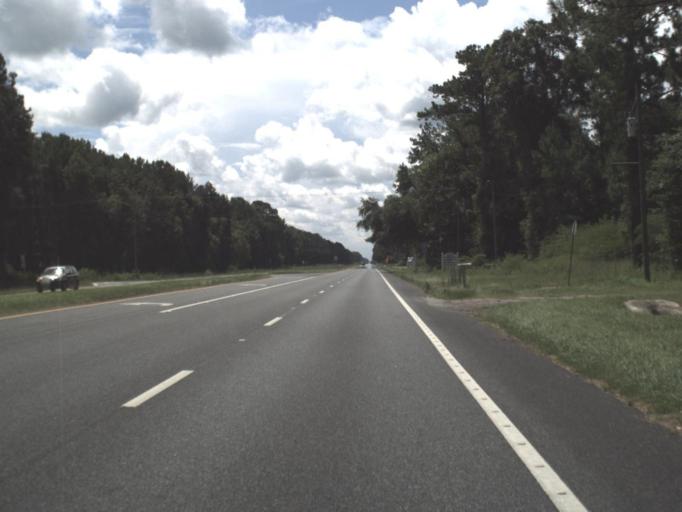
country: US
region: Florida
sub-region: Taylor County
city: Perry
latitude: 30.3027
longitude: -83.7477
